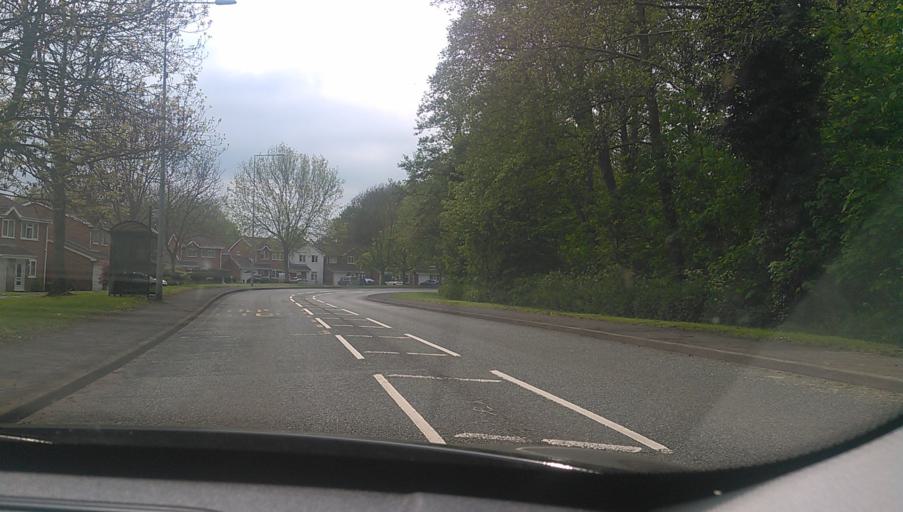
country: GB
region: England
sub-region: Shropshire
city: Hadley
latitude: 52.7153
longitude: -2.4970
